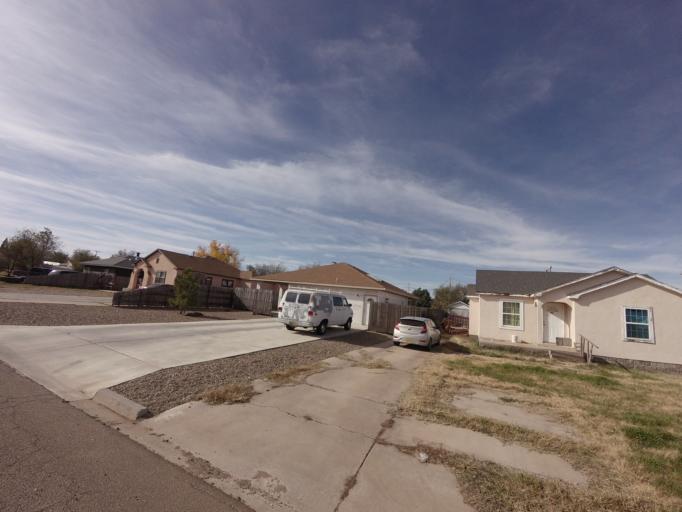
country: US
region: New Mexico
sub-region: Curry County
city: Clovis
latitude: 34.4064
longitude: -103.1927
